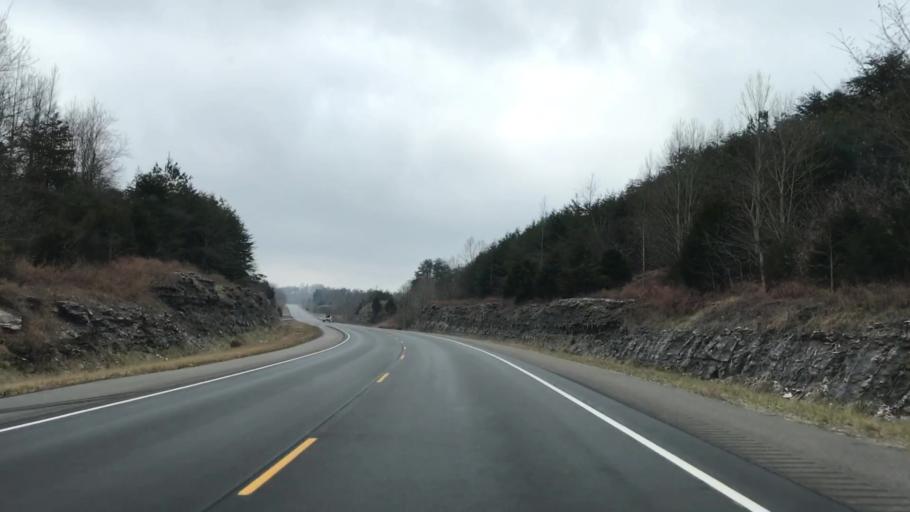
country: US
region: Kentucky
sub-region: Metcalfe County
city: Edmonton
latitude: 36.9513
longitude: -85.4449
